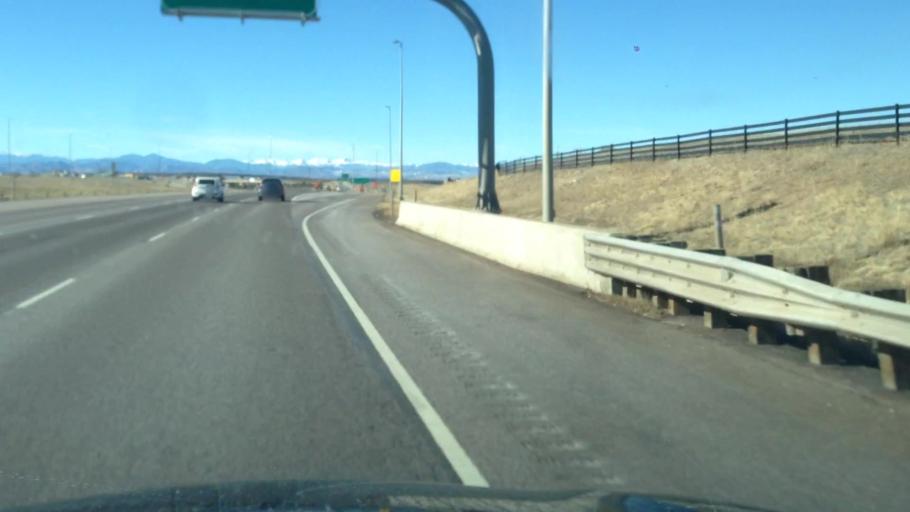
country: US
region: Colorado
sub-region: Douglas County
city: Meridian
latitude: 39.5518
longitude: -104.8555
